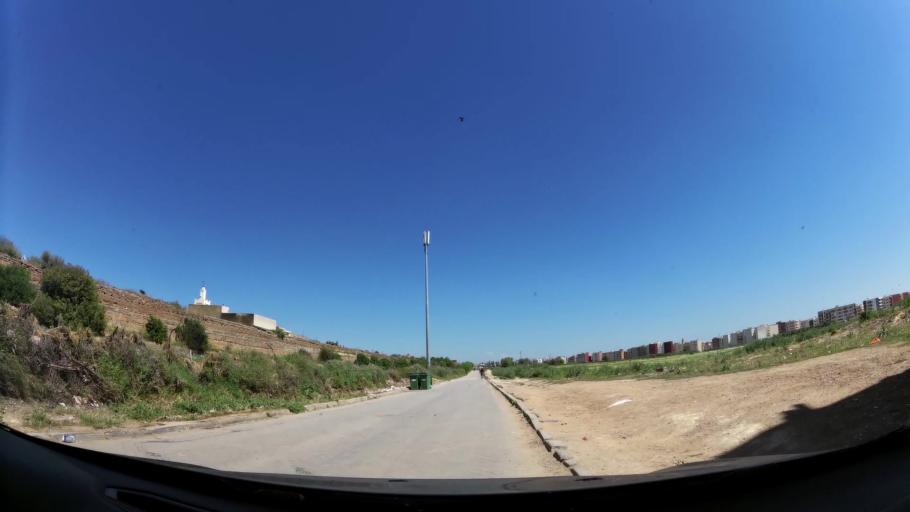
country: MA
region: Meknes-Tafilalet
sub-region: Meknes
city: Meknes
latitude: 33.8656
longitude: -5.5577
